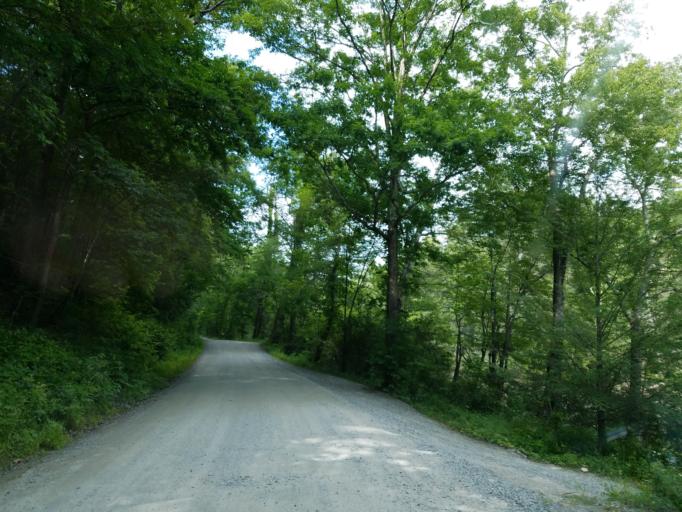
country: US
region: Georgia
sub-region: Fannin County
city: Blue Ridge
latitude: 34.7892
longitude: -84.2538
